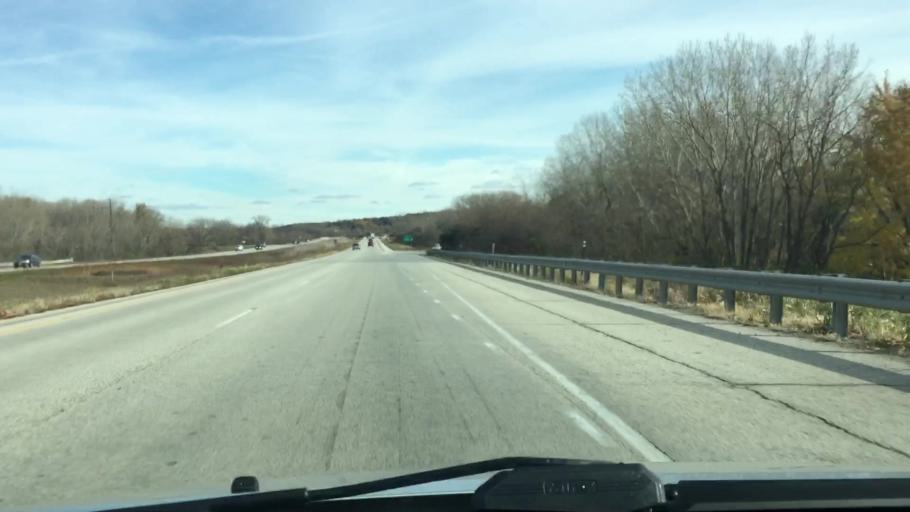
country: US
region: Wisconsin
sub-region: Brown County
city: Green Bay
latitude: 44.5196
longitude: -87.9655
